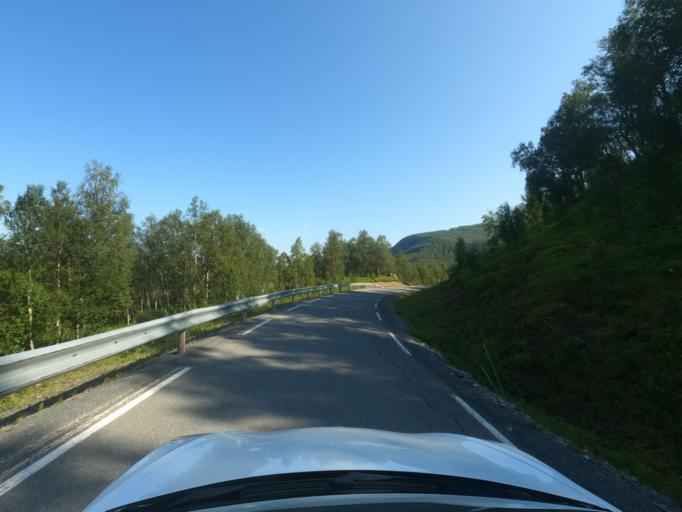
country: NO
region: Troms
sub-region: Skanland
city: Evenskjer
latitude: 68.3306
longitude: 16.5445
